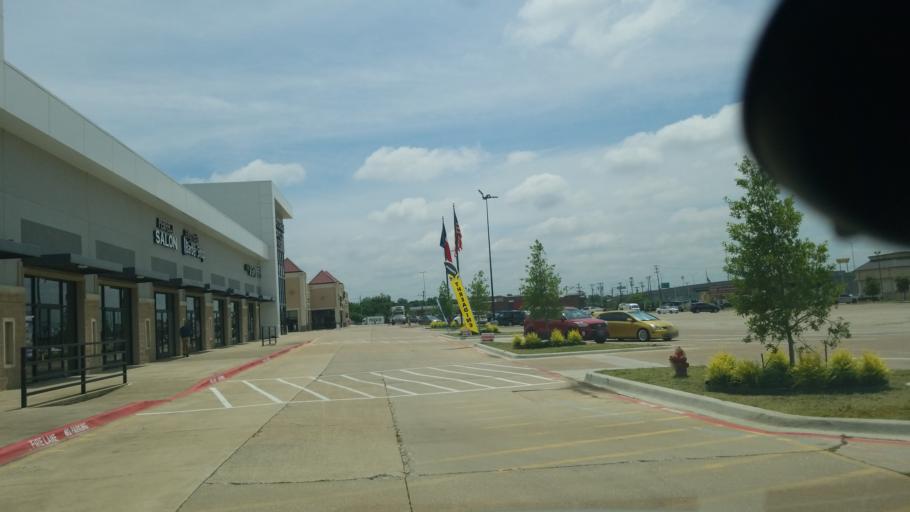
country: US
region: Texas
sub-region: Dallas County
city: Irving
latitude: 32.8391
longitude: -96.9543
